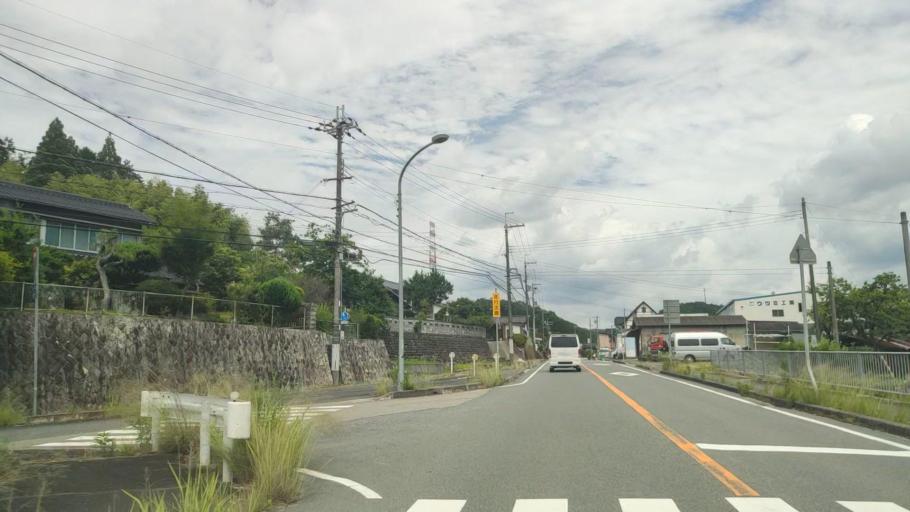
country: JP
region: Hyogo
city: Yamazakicho-nakabirose
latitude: 34.9823
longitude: 134.4200
